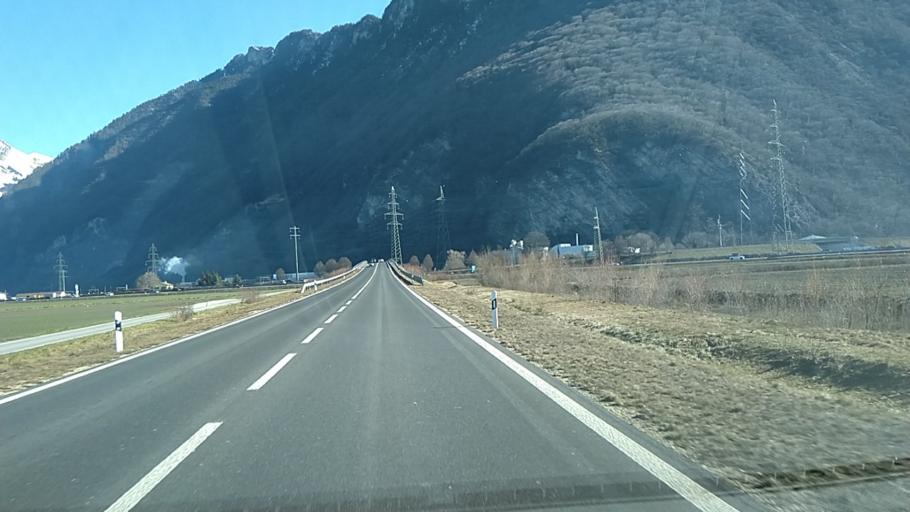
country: CH
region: Vaud
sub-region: Aigle District
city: Villeneuve
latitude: 46.3686
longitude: 6.9190
